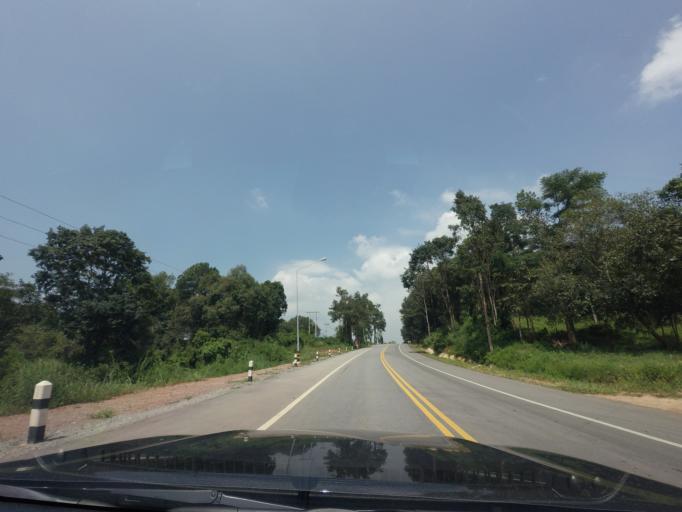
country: TH
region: Loei
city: Phu Ruea
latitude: 17.4558
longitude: 101.4160
